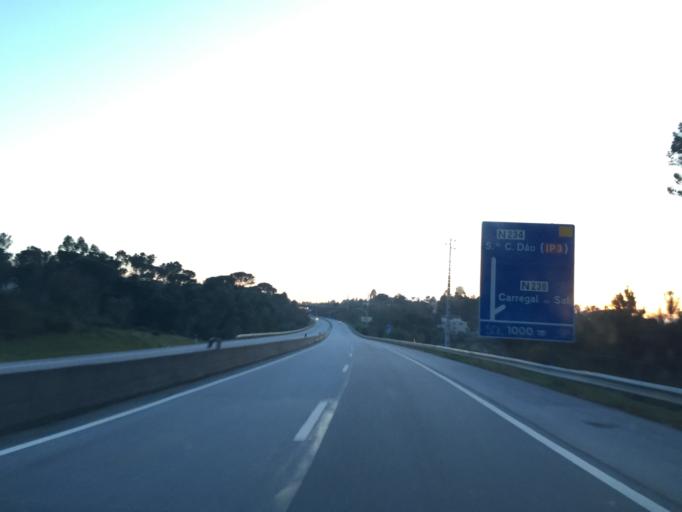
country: PT
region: Viseu
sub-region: Concelho de Carregal do Sal
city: Carregal do Sal
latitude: 40.4380
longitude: -8.0082
